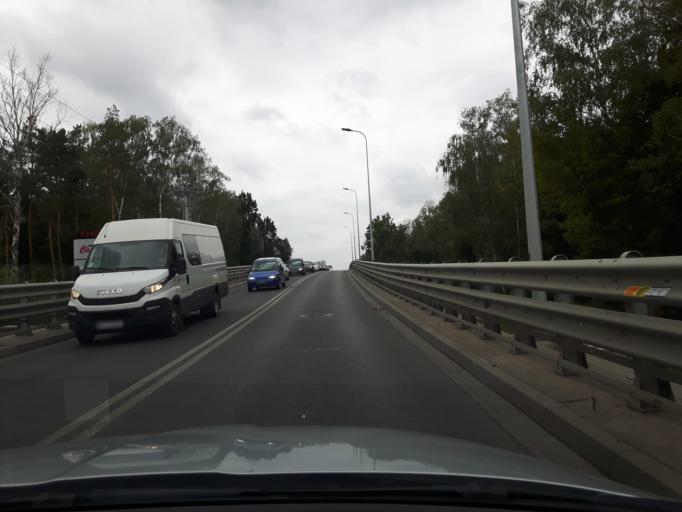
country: PL
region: Masovian Voivodeship
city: Zielonka
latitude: 52.2991
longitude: 21.1500
